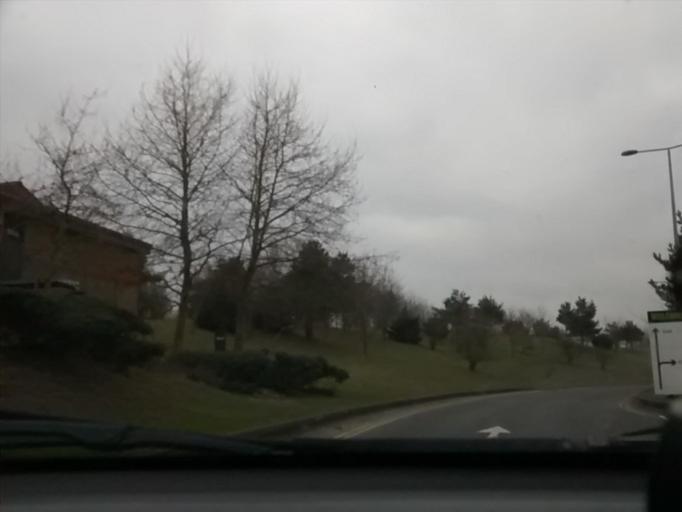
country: GB
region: England
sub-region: Essex
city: Stansted
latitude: 51.8720
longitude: 0.1943
